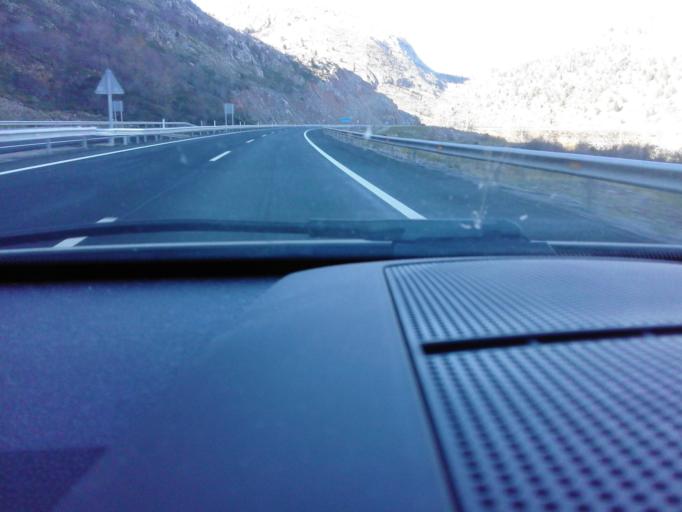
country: ES
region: Castille and Leon
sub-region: Provincia de Leon
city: Sena de Luna
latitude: 42.8804
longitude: -5.8861
